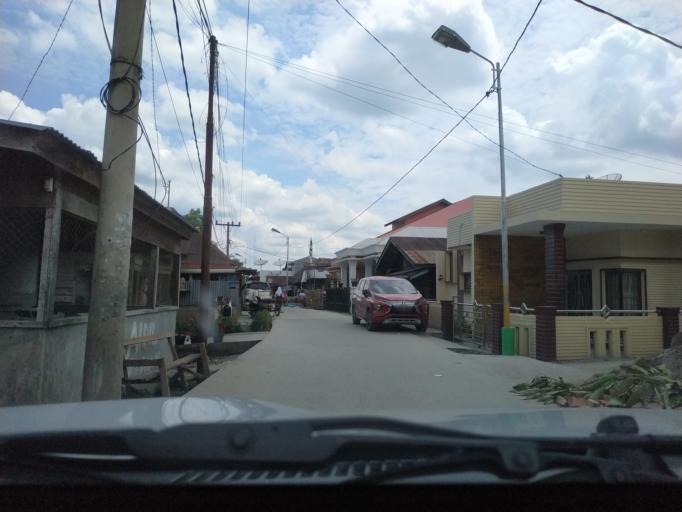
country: ID
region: North Sumatra
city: Tanjungbalai
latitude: 2.9614
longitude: 99.8121
